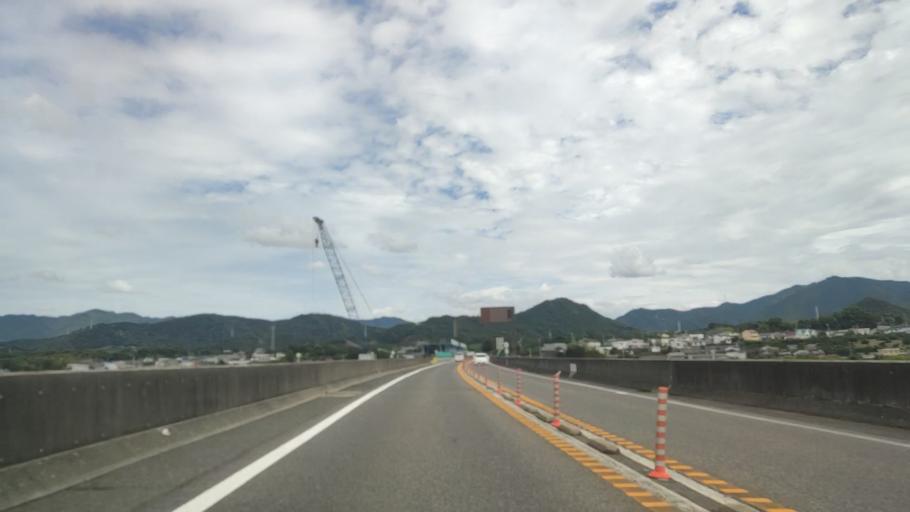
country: JP
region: Wakayama
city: Gobo
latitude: 33.9024
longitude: 135.1876
